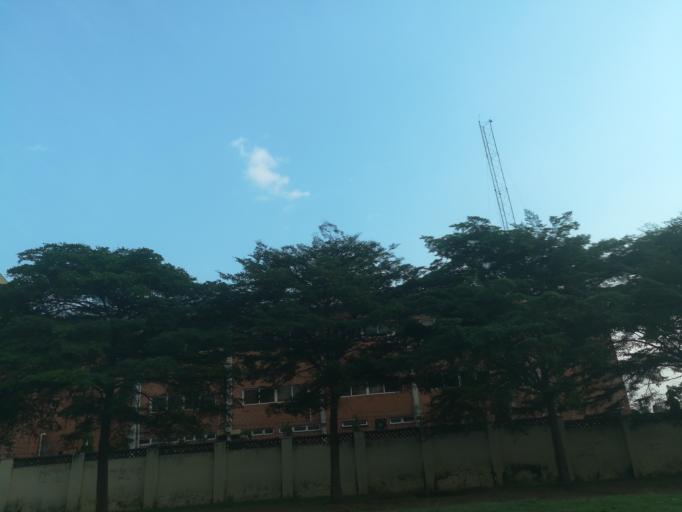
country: NG
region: Abuja Federal Capital Territory
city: Abuja
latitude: 9.0634
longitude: 7.4254
